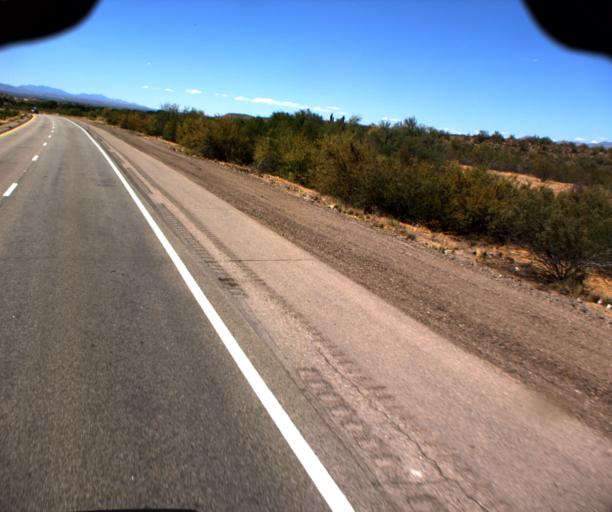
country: US
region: Arizona
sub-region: Yavapai County
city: Bagdad
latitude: 34.6582
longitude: -113.5765
